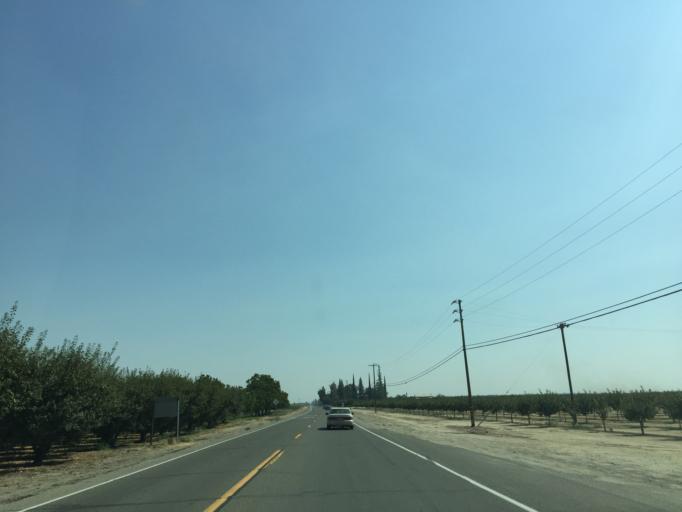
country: US
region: California
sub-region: Kings County
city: Lucerne
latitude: 36.4003
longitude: -119.6730
